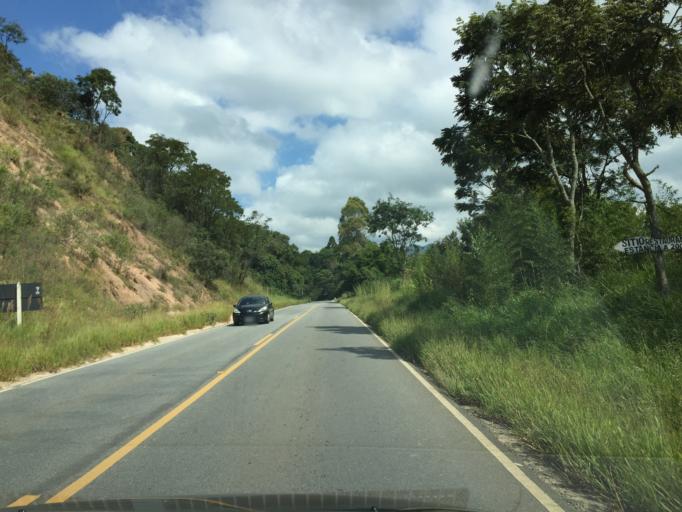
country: BR
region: Minas Gerais
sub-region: Passa Quatro
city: Passa Quatro
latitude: -22.3771
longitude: -44.9637
